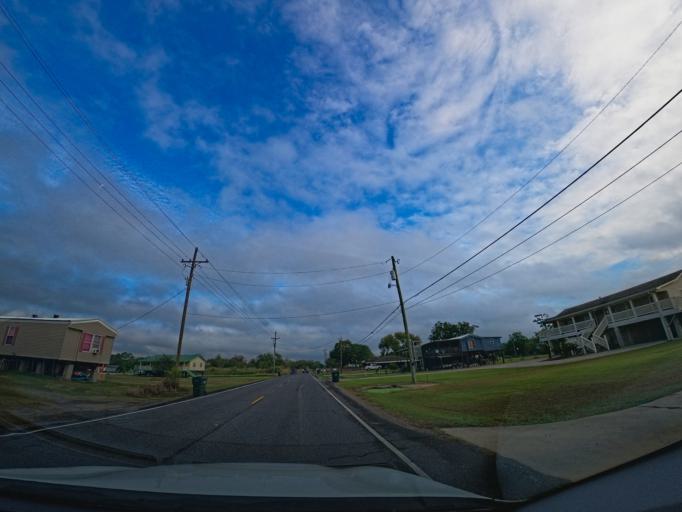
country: US
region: Louisiana
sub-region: Terrebonne Parish
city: Dulac
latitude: 29.4406
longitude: -90.7025
